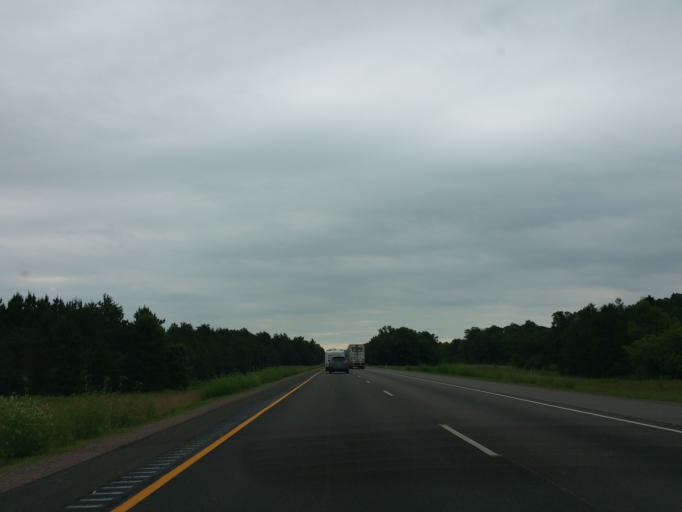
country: US
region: Wisconsin
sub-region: Trempealeau County
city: Osseo
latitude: 44.5555
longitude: -91.1743
